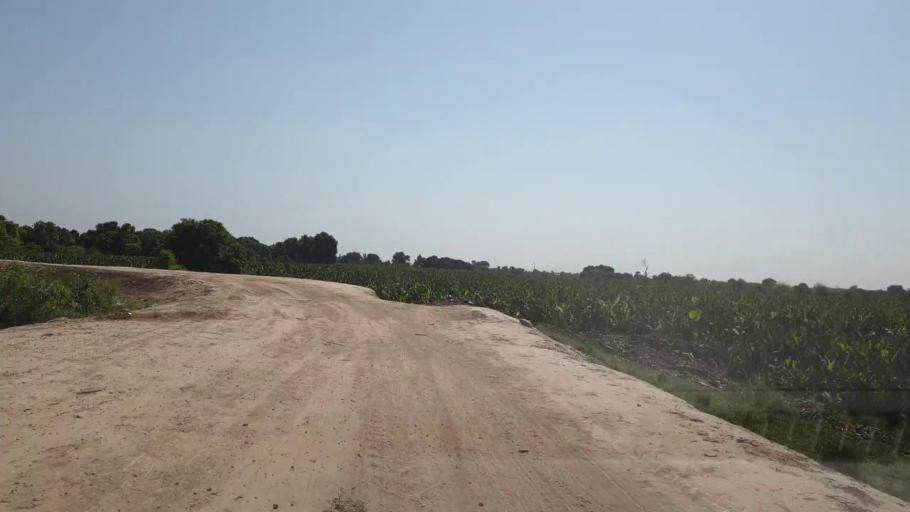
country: PK
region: Sindh
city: Matiari
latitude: 25.6276
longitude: 68.4780
